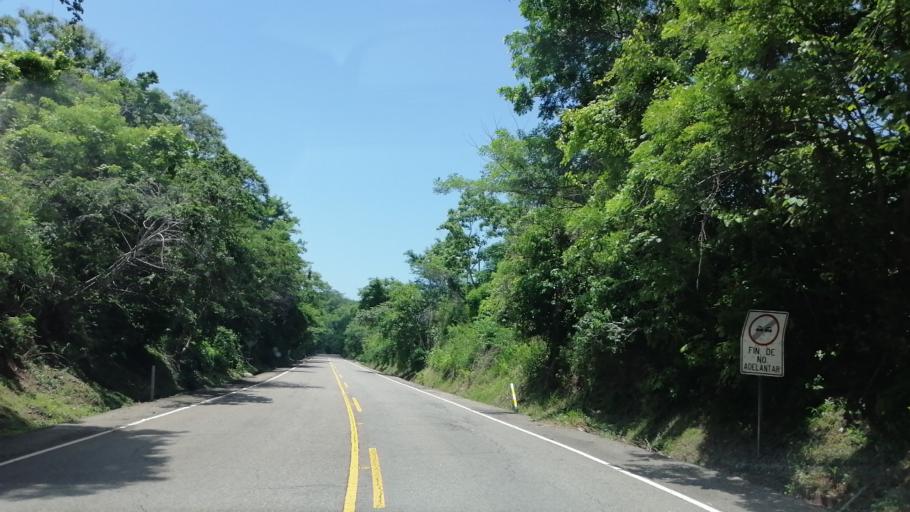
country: SV
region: Chalatenango
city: Nueva Concepcion
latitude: 14.1783
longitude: -89.3212
